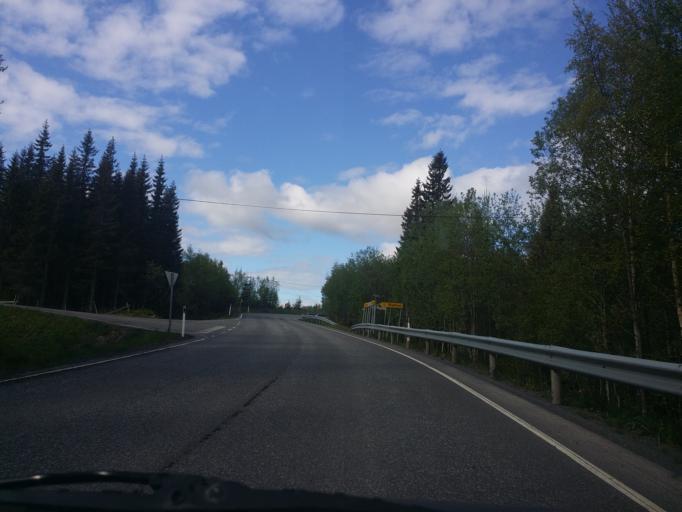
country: NO
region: Hedmark
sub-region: Ringsaker
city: Moelv
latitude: 61.0946
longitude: 10.6557
